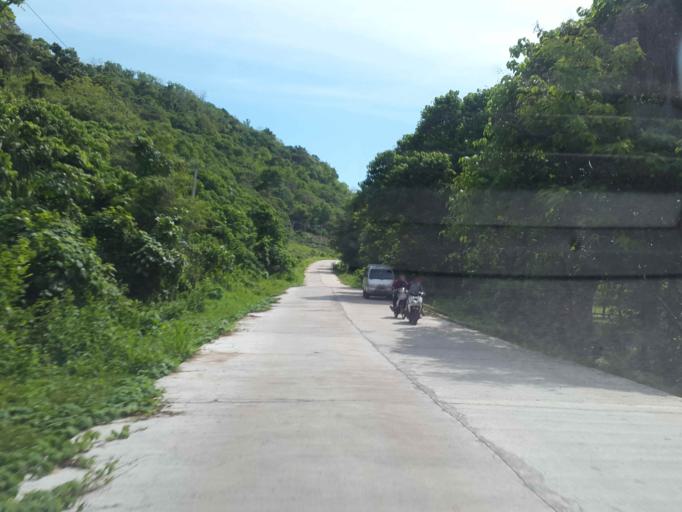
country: ID
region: Banten
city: Citeureup
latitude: -6.5060
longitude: 105.6392
